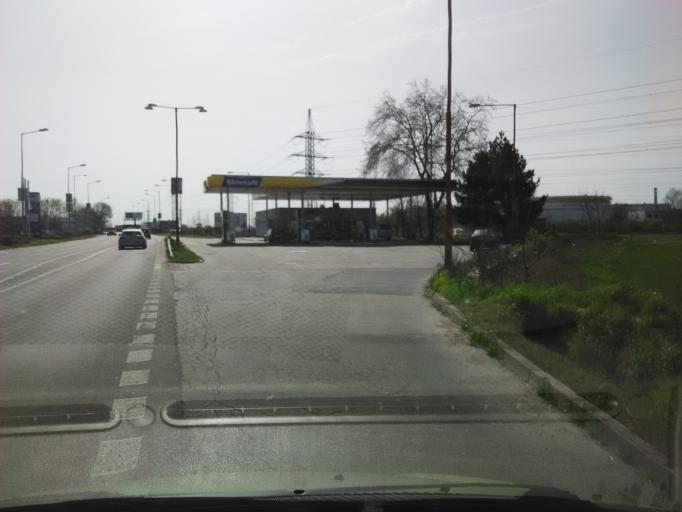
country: SK
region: Bratislavsky
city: Dunajska Luzna
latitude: 48.1298
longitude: 17.1943
